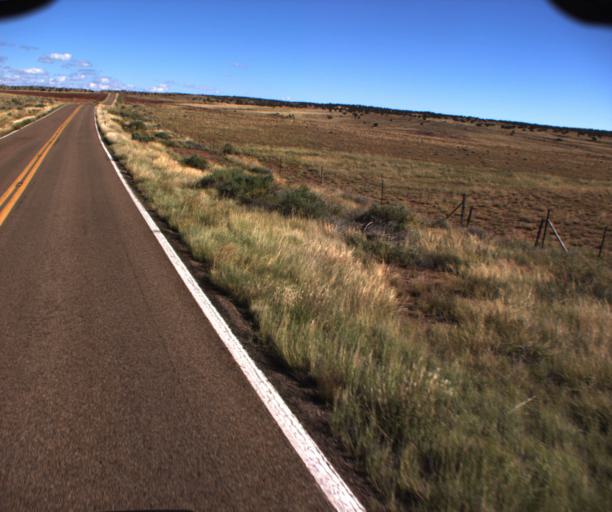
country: US
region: Arizona
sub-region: Apache County
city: Saint Johns
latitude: 34.6388
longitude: -109.3077
